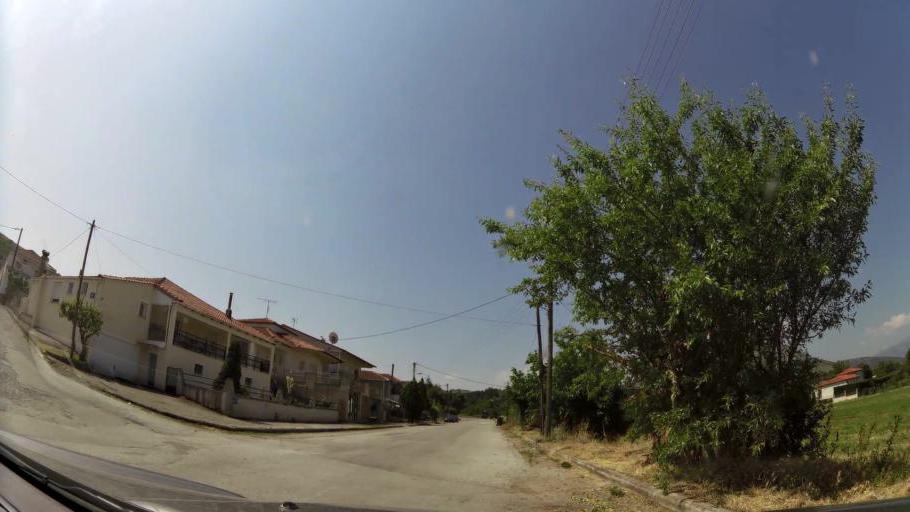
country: GR
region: West Macedonia
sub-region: Nomos Kozanis
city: Koila
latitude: 40.3275
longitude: 21.7917
